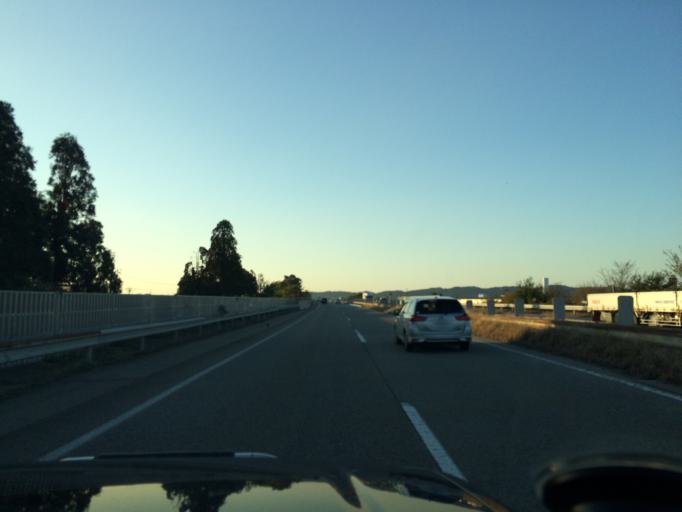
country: JP
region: Toyama
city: Toyama-shi
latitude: 36.6594
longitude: 137.1990
